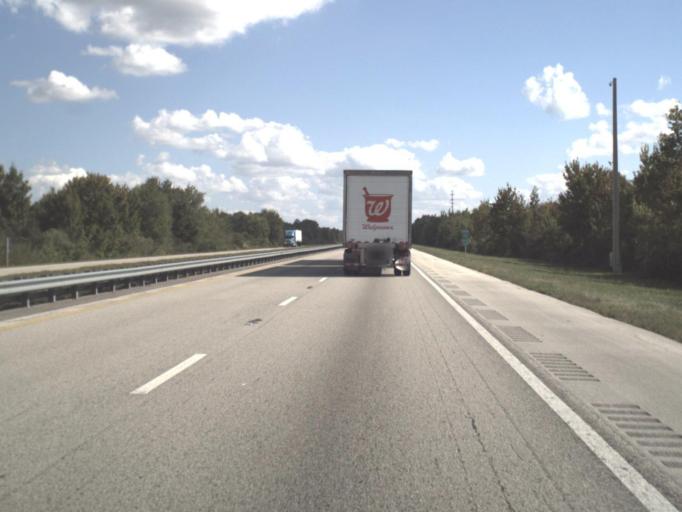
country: US
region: Florida
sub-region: Osceola County
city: Saint Cloud
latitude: 28.0356
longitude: -81.1999
